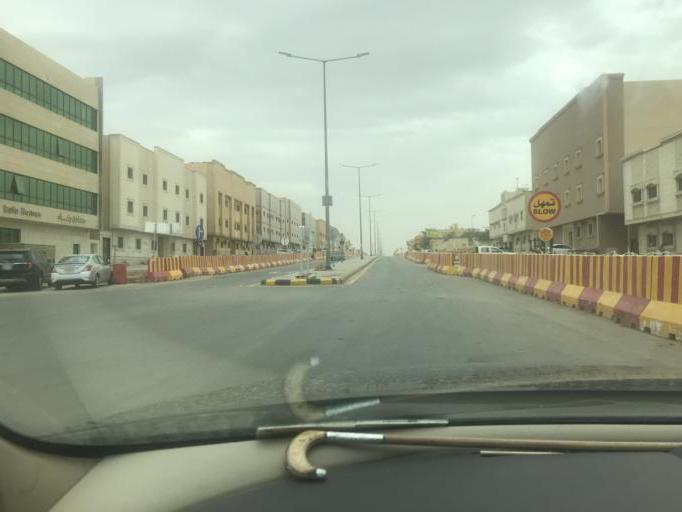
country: SA
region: Ar Riyad
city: Riyadh
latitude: 24.7954
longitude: 46.7086
